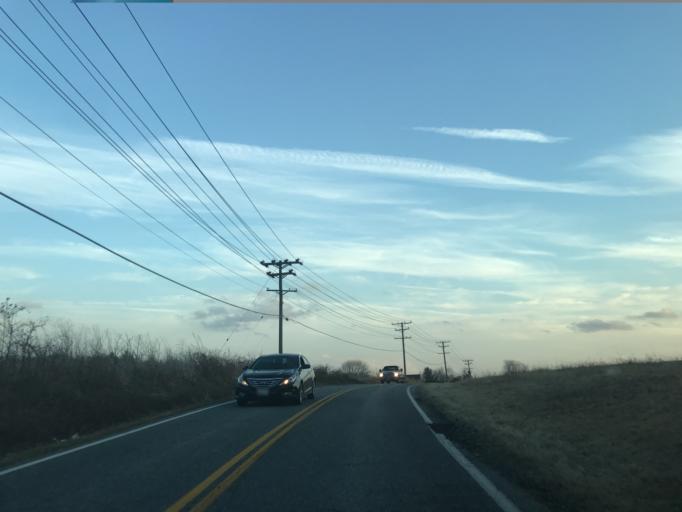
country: US
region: Maryland
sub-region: Harford County
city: Bel Air South
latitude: 39.5259
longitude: -76.2770
